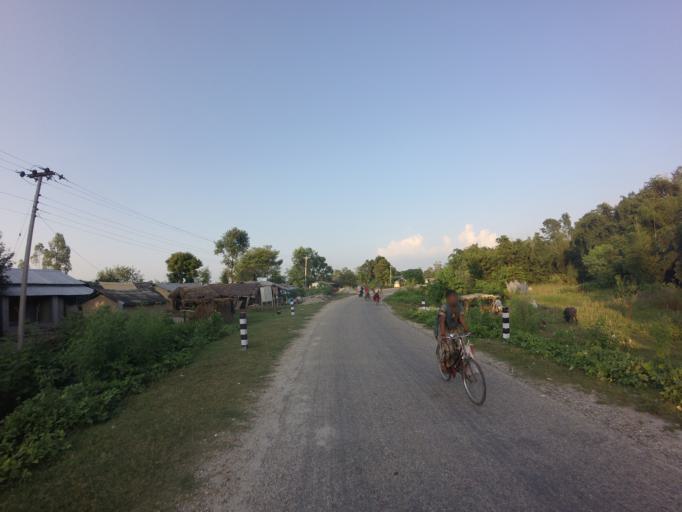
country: NP
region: Far Western
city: Tikapur
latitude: 28.4550
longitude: 81.0738
